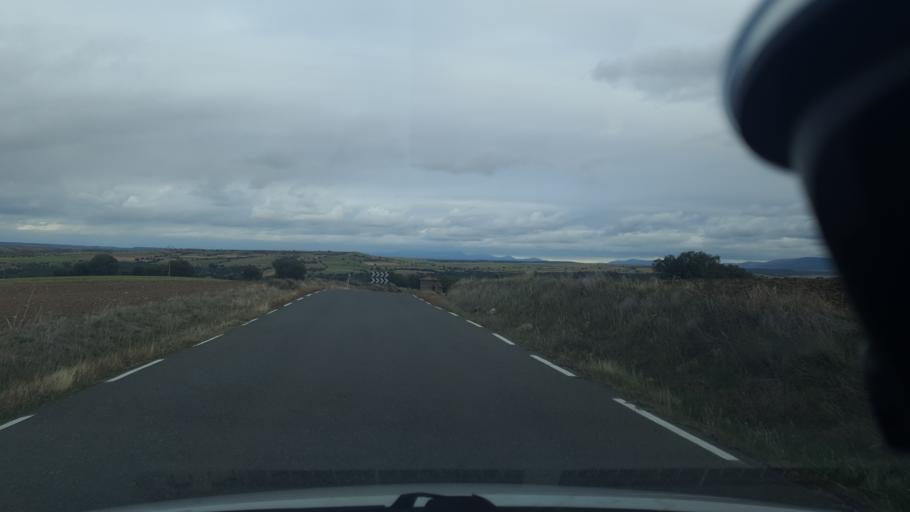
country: ES
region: Castille and Leon
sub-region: Provincia de Avila
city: Gotarrendura
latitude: 40.8261
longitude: -4.7110
